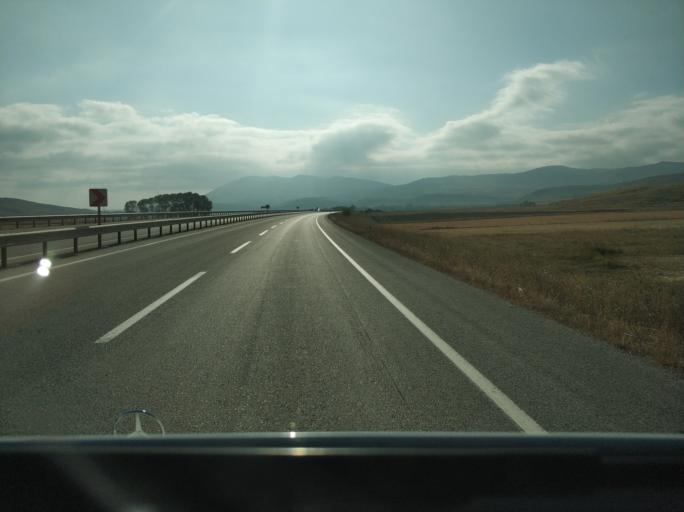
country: TR
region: Sivas
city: Yildizeli
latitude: 39.8510
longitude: 36.5056
